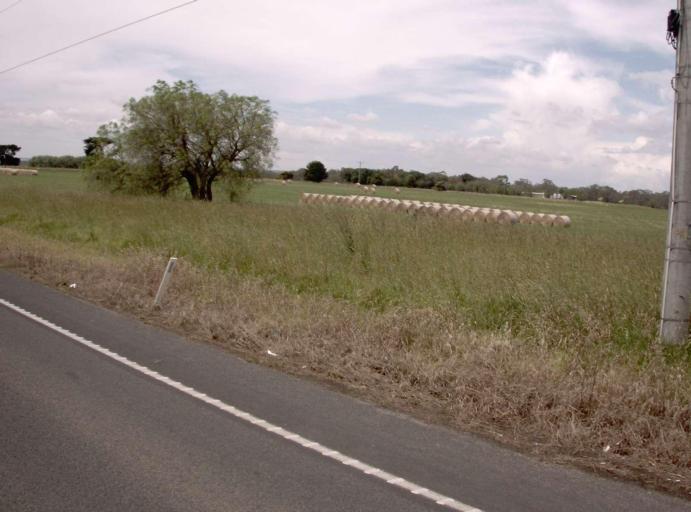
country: AU
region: Victoria
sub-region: Wellington
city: Sale
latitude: -38.0691
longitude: 147.0352
